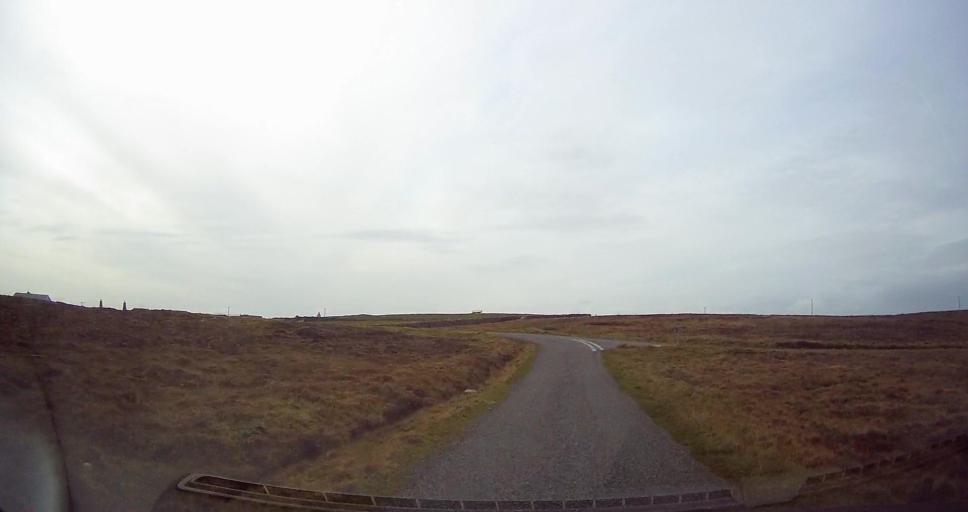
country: GB
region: Scotland
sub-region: Shetland Islands
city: Shetland
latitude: 60.1529
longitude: -1.0929
